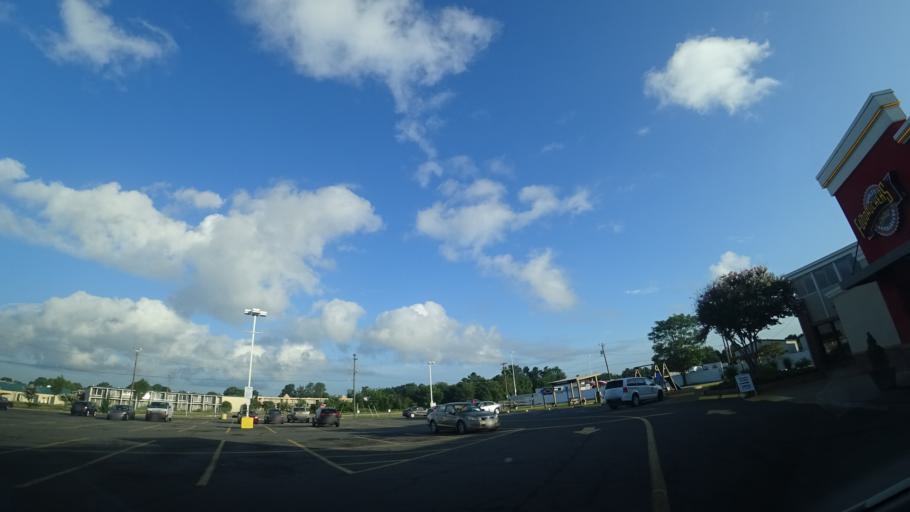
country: US
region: Virginia
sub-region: Hanover County
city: Ashland
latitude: 37.7596
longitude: -77.4633
